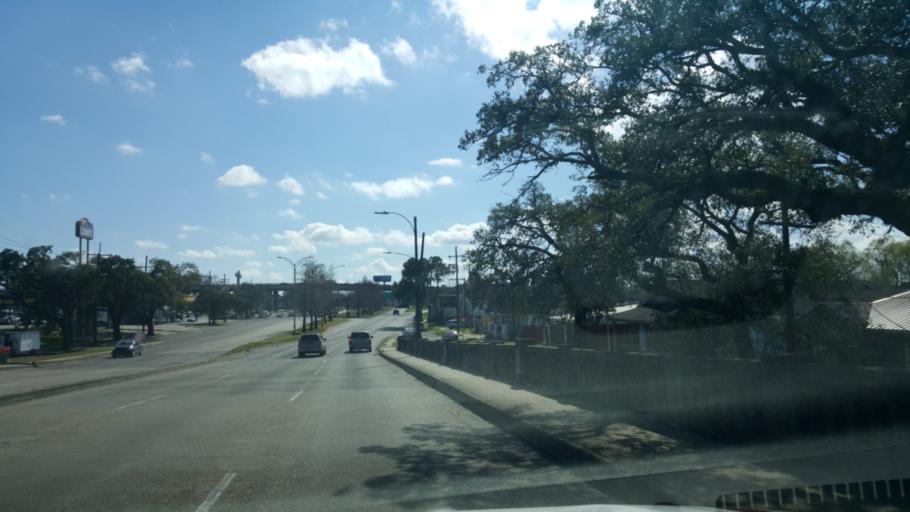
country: US
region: Louisiana
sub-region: Orleans Parish
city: New Orleans
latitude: 29.9845
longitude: -90.0582
